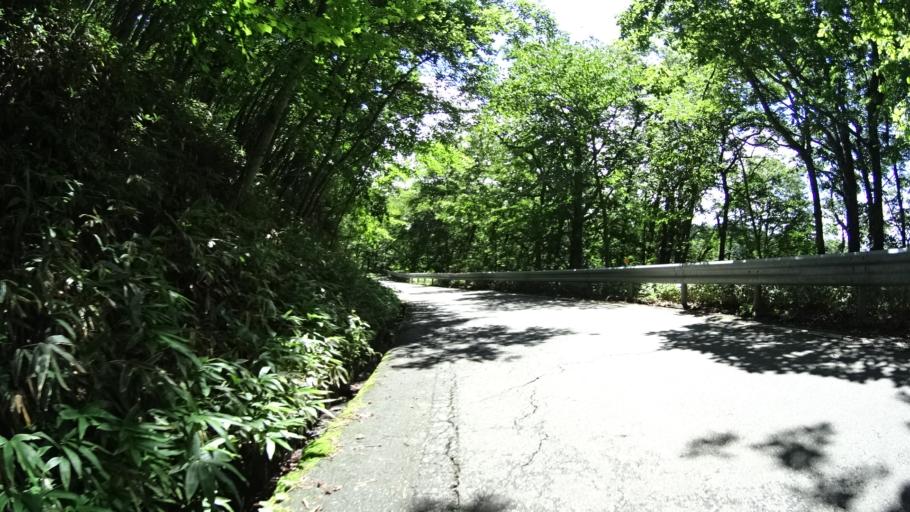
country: JP
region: Yamanashi
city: Enzan
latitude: 35.7339
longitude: 138.8315
